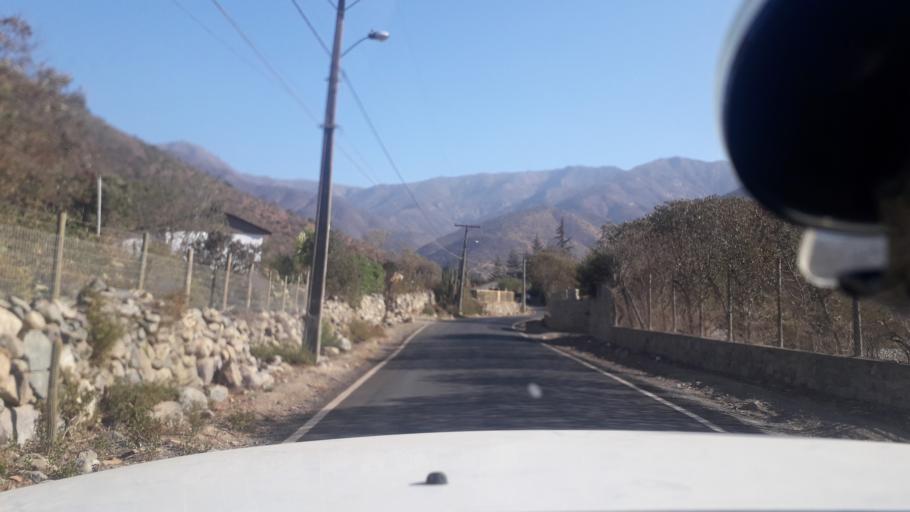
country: CL
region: Valparaiso
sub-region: Provincia de Marga Marga
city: Limache
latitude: -33.0549
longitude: -71.1121
